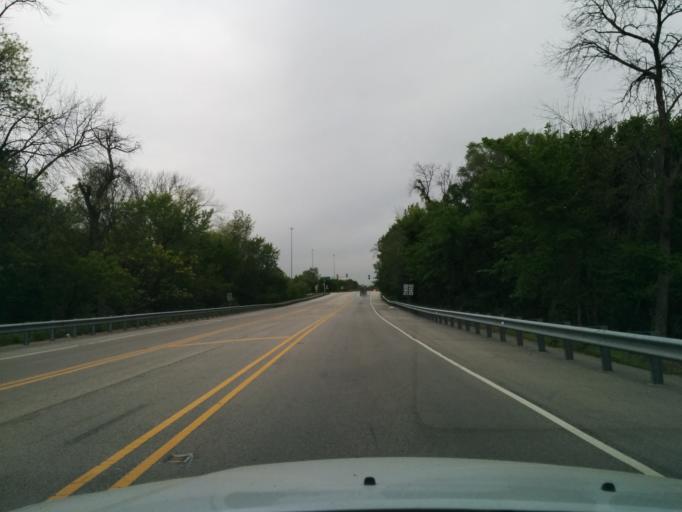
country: US
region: Illinois
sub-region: Cook County
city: Palos Park
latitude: 41.6830
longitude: -87.8511
